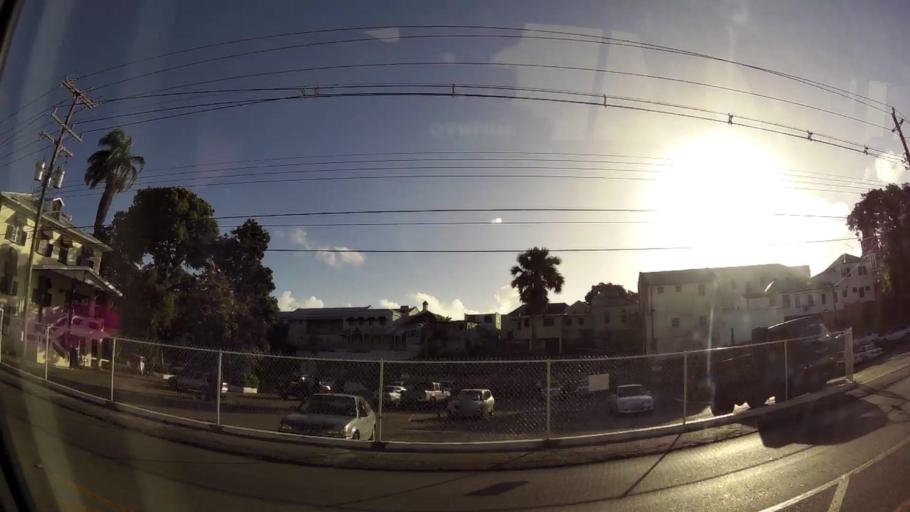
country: BB
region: Saint Michael
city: Bridgetown
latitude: 13.0810
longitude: -59.6076
